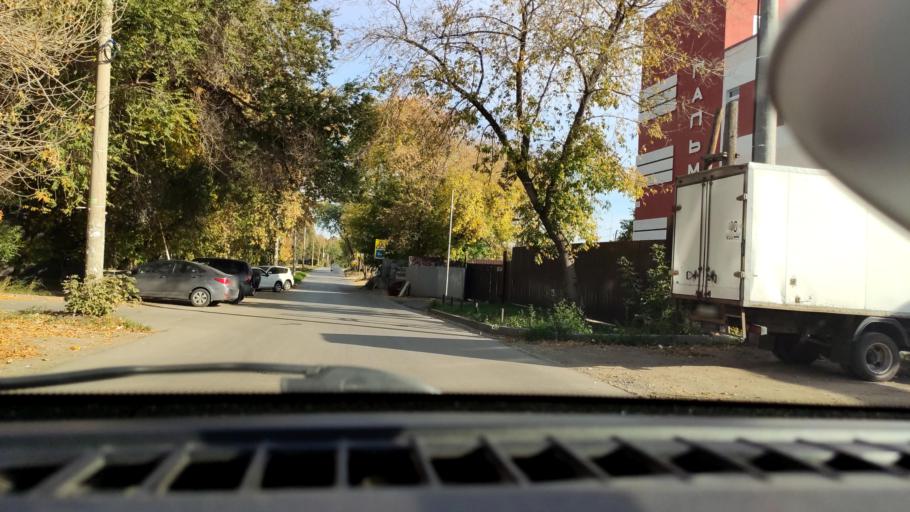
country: RU
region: Samara
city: Samara
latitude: 53.1849
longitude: 50.1939
